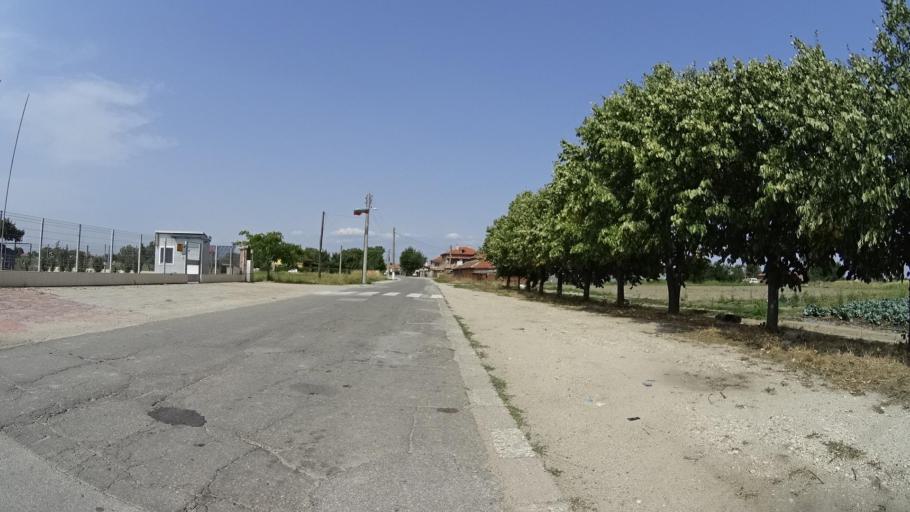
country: BG
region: Plovdiv
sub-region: Obshtina Plovdiv
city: Plovdiv
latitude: 42.2368
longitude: 24.7888
